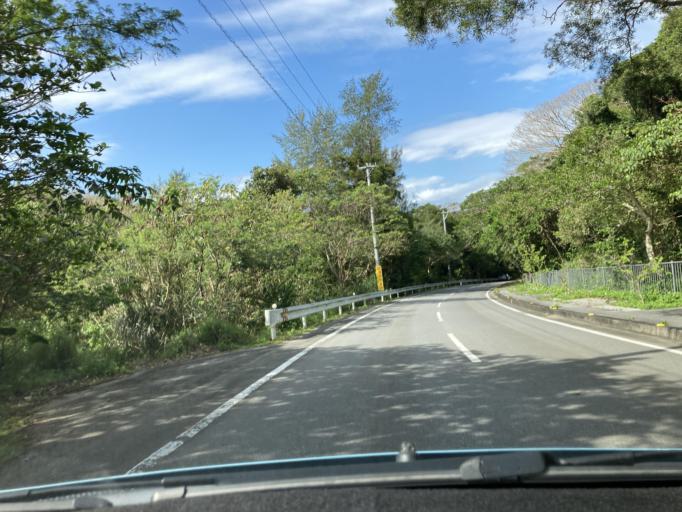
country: JP
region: Okinawa
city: Nago
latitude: 26.6928
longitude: 127.9254
